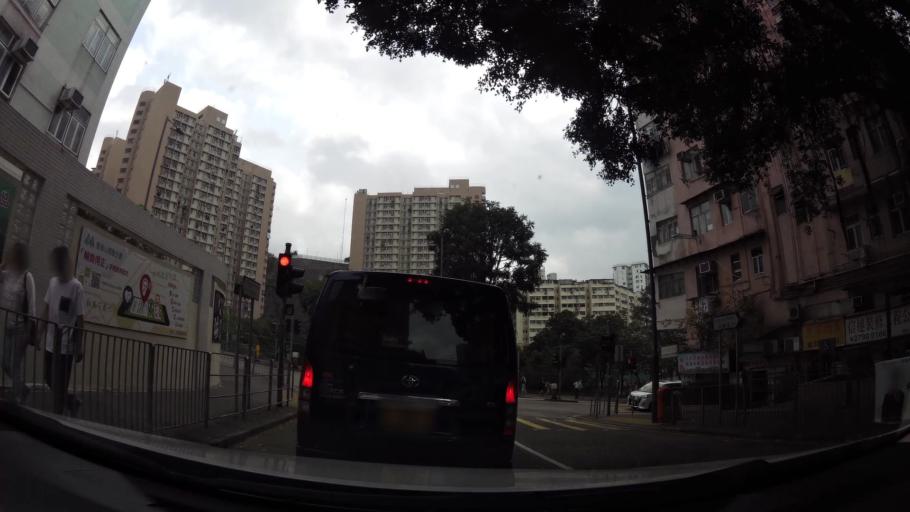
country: HK
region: Kowloon City
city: Kowloon
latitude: 22.3173
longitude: 114.2226
